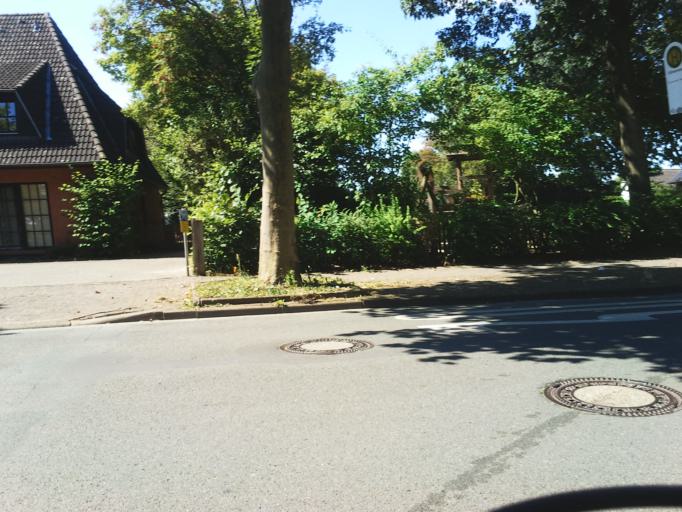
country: DE
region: Lower Saxony
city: Nienburg
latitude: 52.6648
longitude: 9.2266
